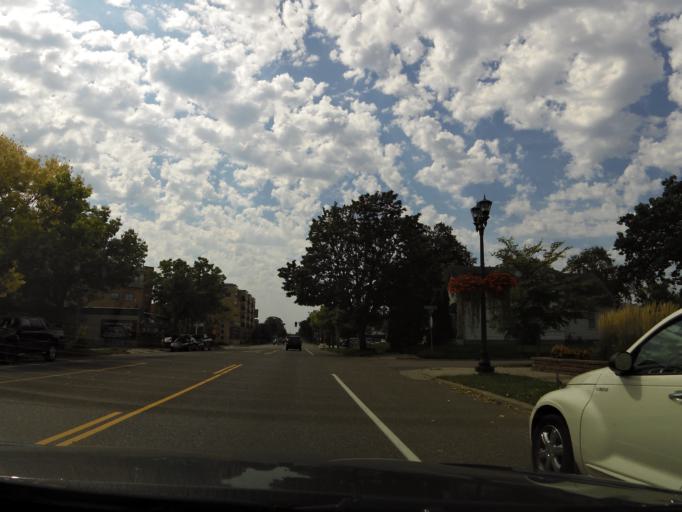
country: US
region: Minnesota
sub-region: Dakota County
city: West Saint Paul
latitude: 44.9204
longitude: -93.1376
